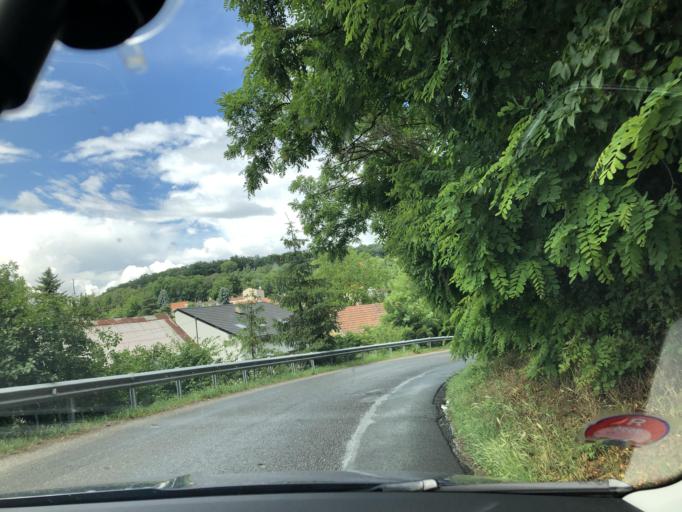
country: CZ
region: Central Bohemia
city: Nelahozeves
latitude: 50.2599
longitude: 14.2961
